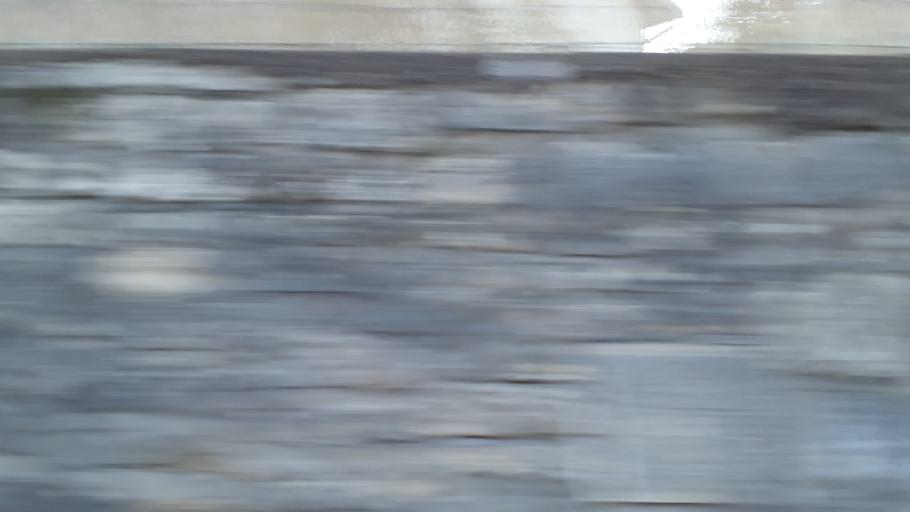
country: FR
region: Franche-Comte
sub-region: Departement du Doubs
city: Novillars
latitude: 47.2837
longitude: 6.1524
